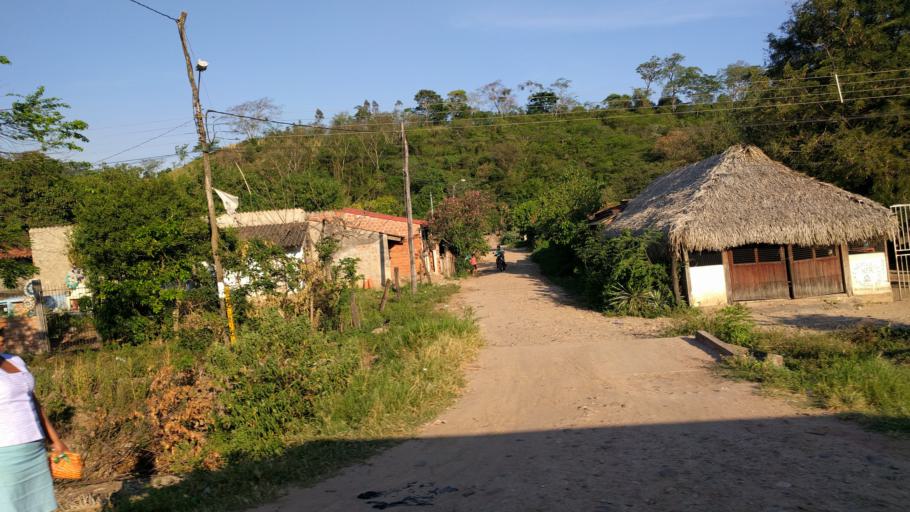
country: BO
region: Santa Cruz
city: Limoncito
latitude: -18.0124
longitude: -63.3937
